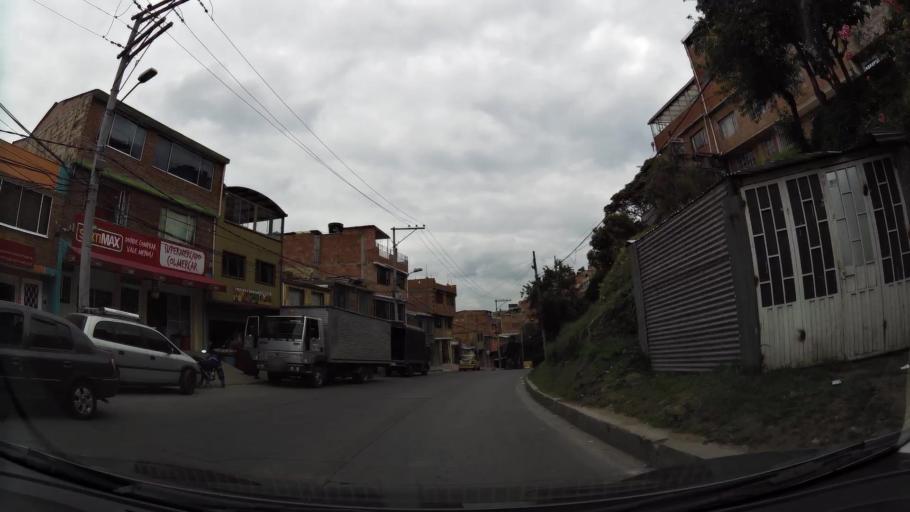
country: CO
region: Cundinamarca
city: La Calera
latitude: 4.7665
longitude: -74.0266
